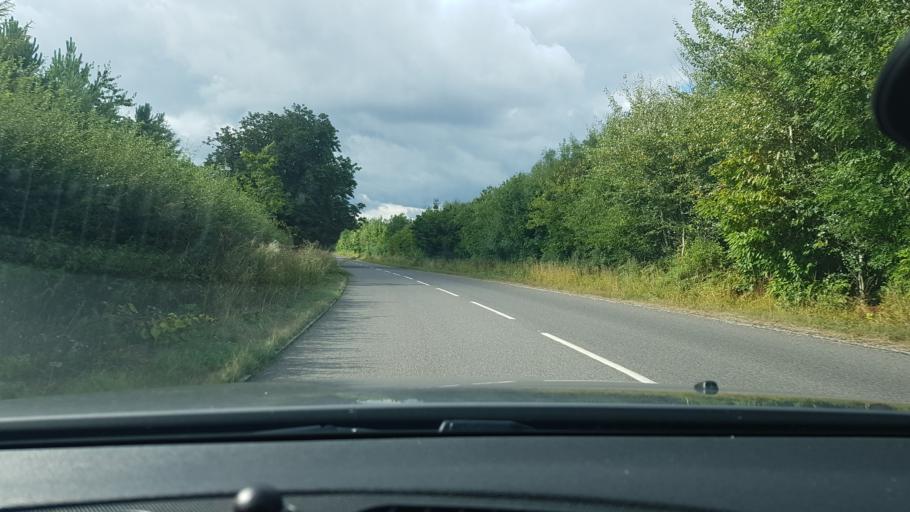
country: GB
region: England
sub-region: West Berkshire
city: Wickham
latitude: 51.4375
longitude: -1.4199
